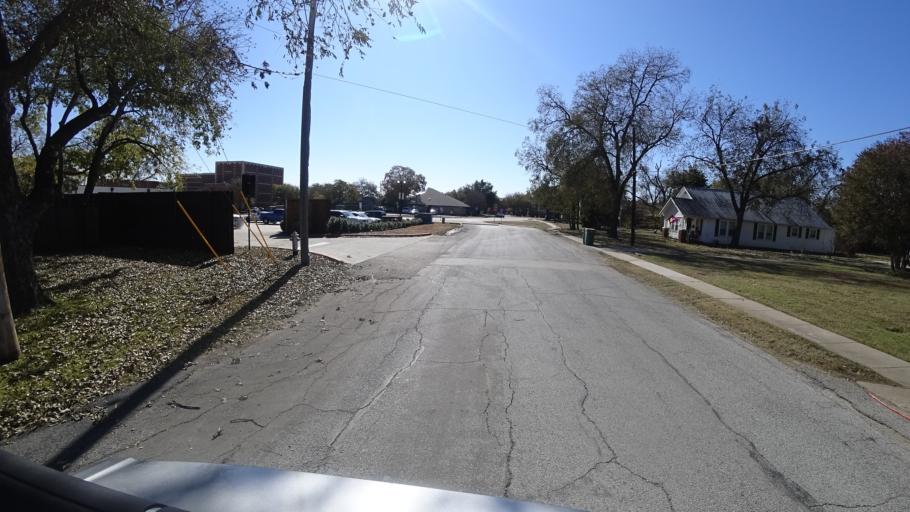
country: US
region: Texas
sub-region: Denton County
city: Lewisville
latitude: 33.0475
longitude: -96.9982
